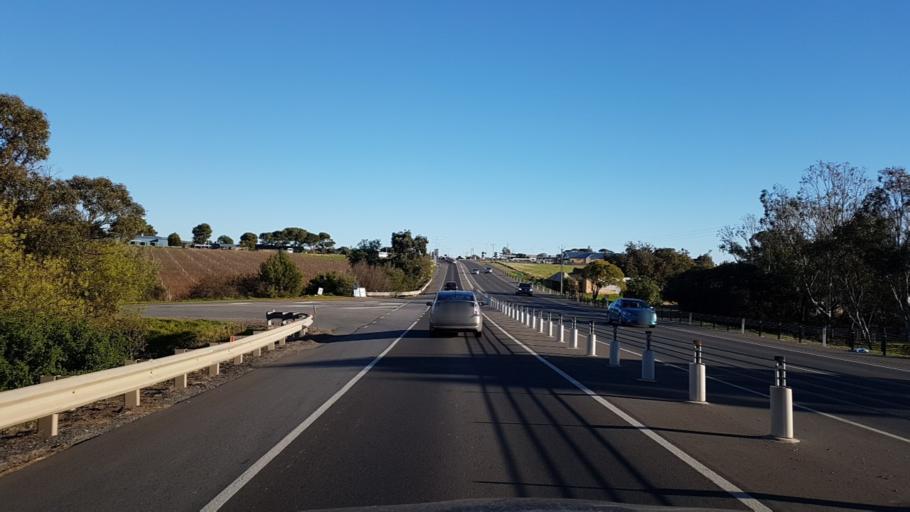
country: AU
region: South Australia
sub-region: Onkaparinga
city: Aldinga
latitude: -35.2639
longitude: 138.4878
